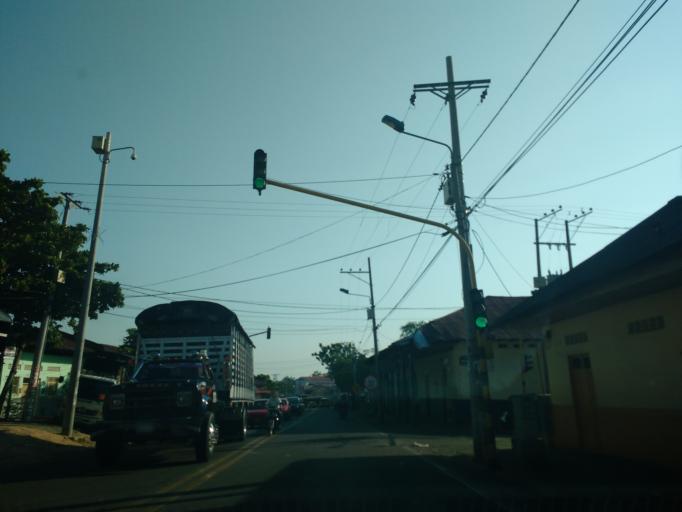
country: CO
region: Cundinamarca
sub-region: Girardot
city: Girardot City
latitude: 4.2914
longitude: -74.8064
